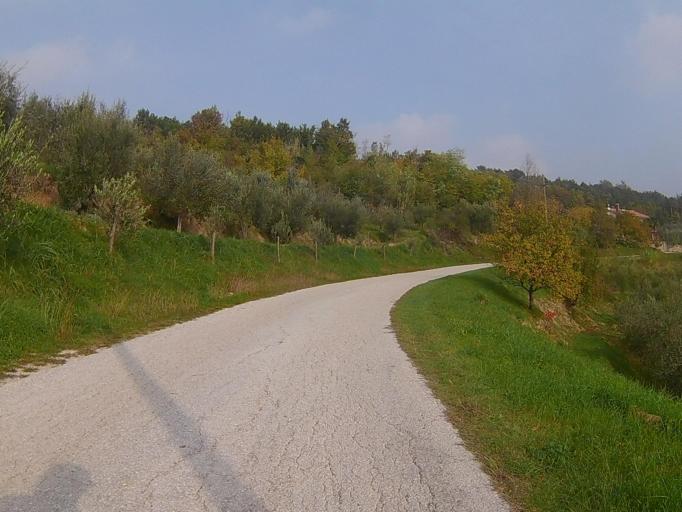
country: HR
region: Istarska
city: Buje
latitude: 45.3830
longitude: 13.6918
